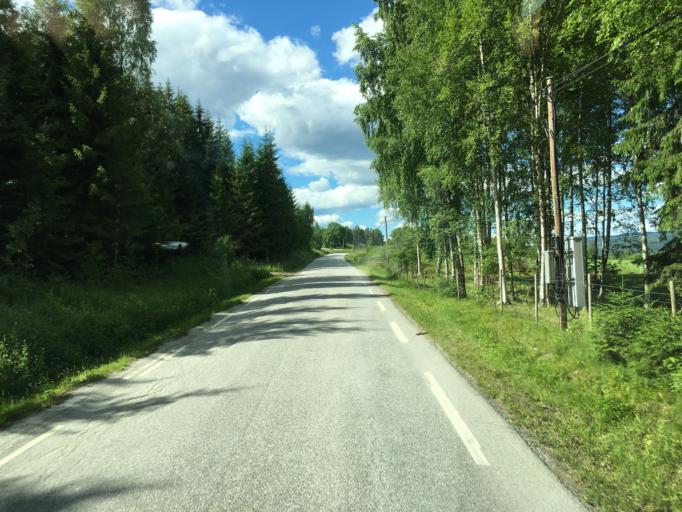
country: NO
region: Oppland
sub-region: Sondre Land
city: Hov
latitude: 60.6839
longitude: 10.3075
